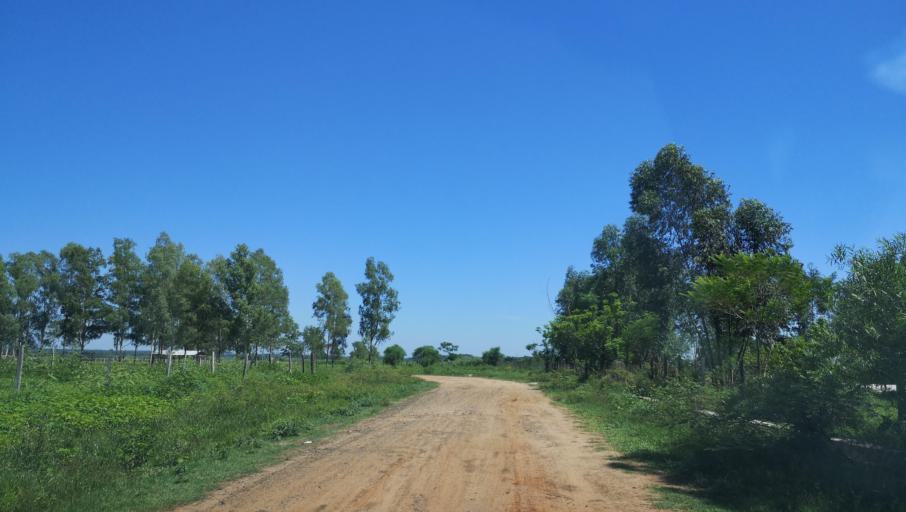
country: PY
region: Caaguazu
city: Carayao
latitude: -25.1975
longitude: -56.4040
